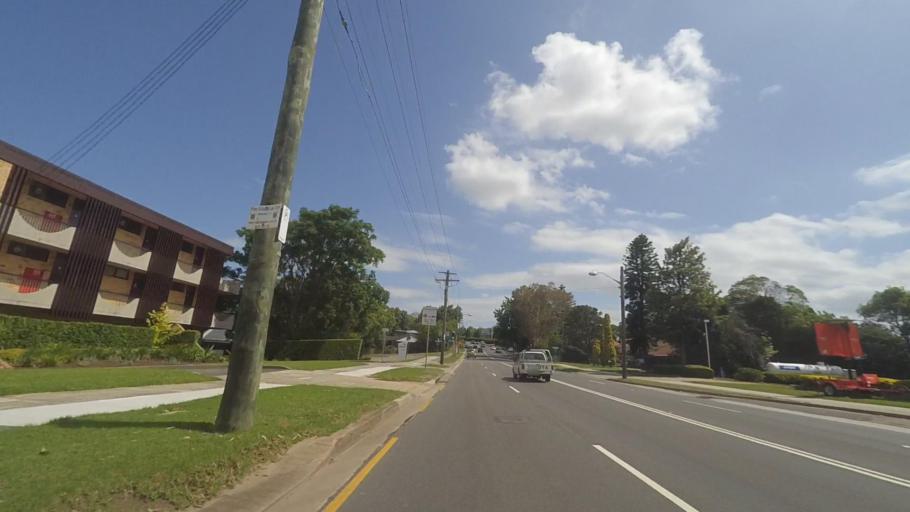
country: AU
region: New South Wales
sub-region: The Hills Shire
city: West Pennant
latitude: -33.7637
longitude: 151.0477
